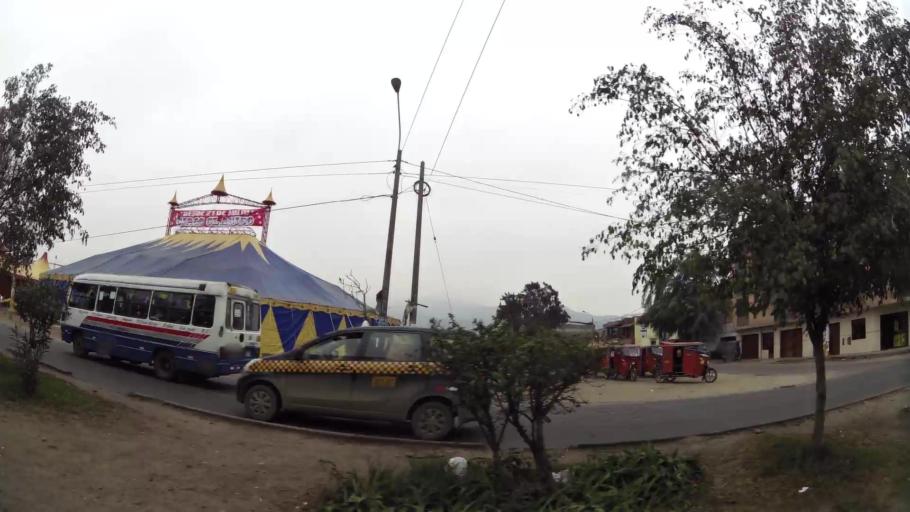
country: PE
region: Lima
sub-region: Lima
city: Independencia
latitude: -11.9768
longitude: -77.0099
